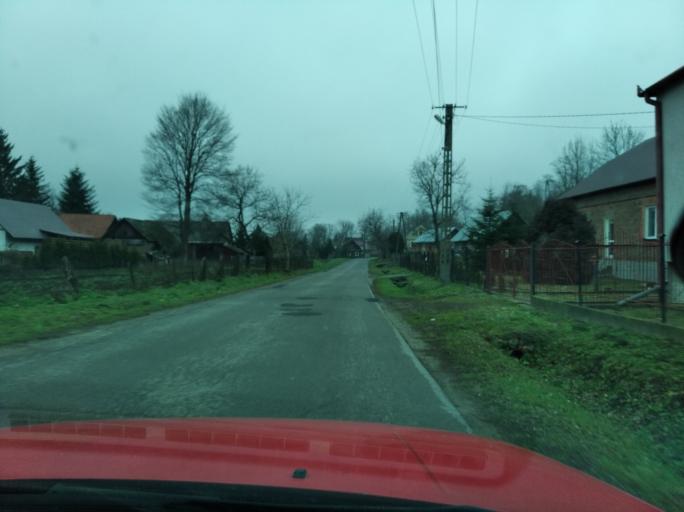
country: PL
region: Subcarpathian Voivodeship
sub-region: Powiat przeworski
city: Rozborz
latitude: 50.0627
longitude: 22.5395
